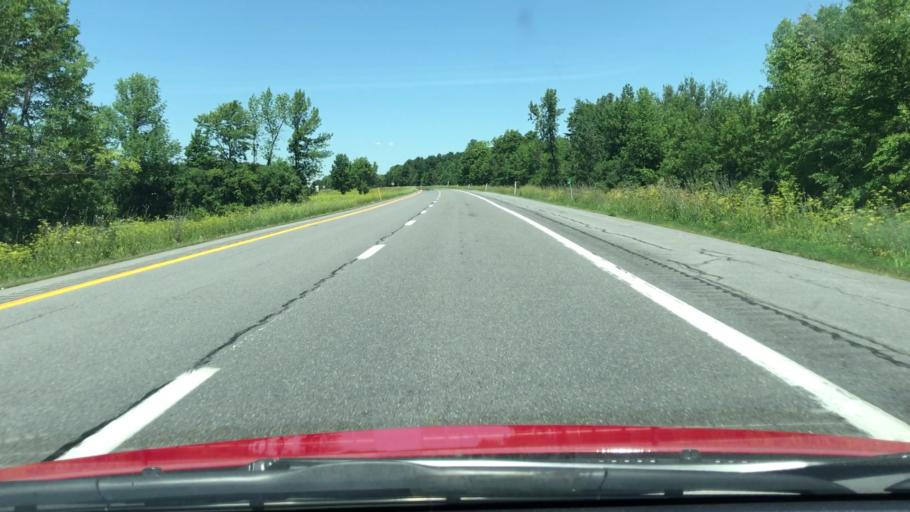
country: US
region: New York
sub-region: Clinton County
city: Champlain
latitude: 44.9200
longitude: -73.4462
